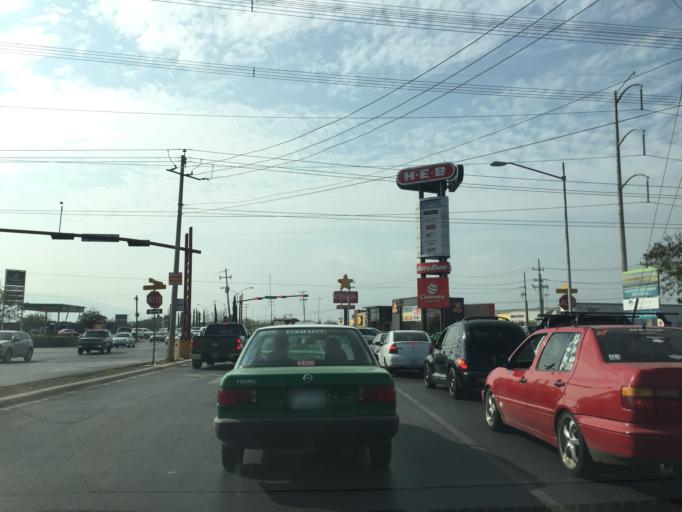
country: MX
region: Nuevo Leon
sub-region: Apodaca
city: Fraccionamiento Cosmopolis Octavo Sector
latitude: 25.7837
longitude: -100.2241
